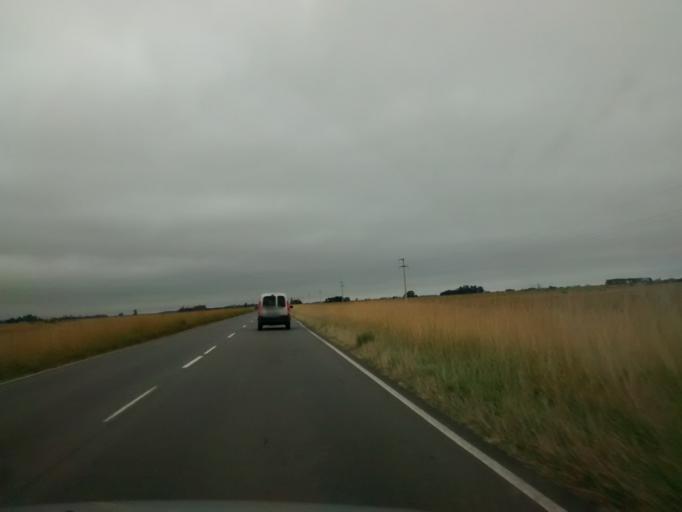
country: AR
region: Buenos Aires
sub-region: Partido de Ayacucho
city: Ayacucho
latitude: -37.0174
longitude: -58.5382
